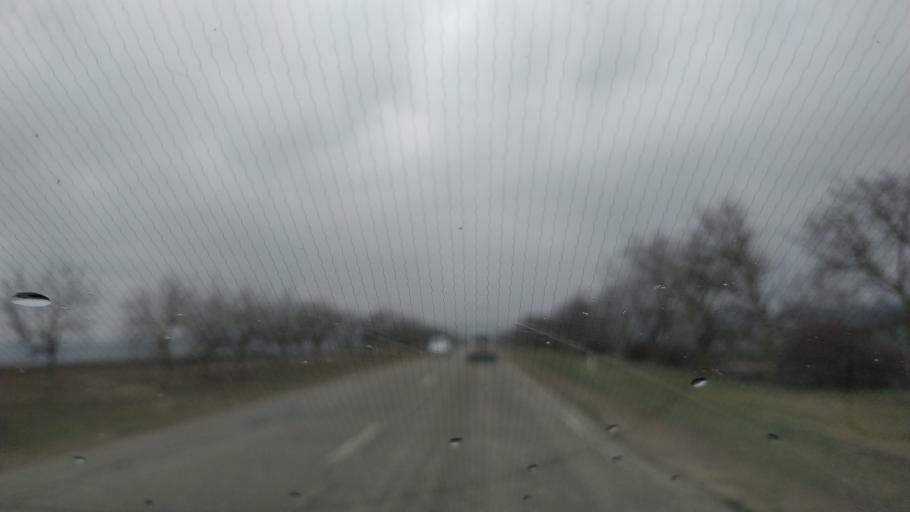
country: MD
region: Gagauzia
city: Comrat
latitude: 46.2517
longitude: 28.7572
